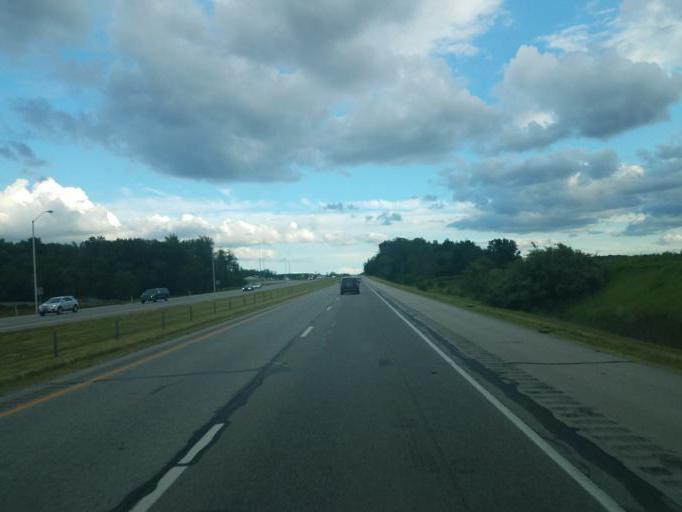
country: US
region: Indiana
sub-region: DeKalb County
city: Garrett
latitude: 41.3012
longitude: -85.0876
